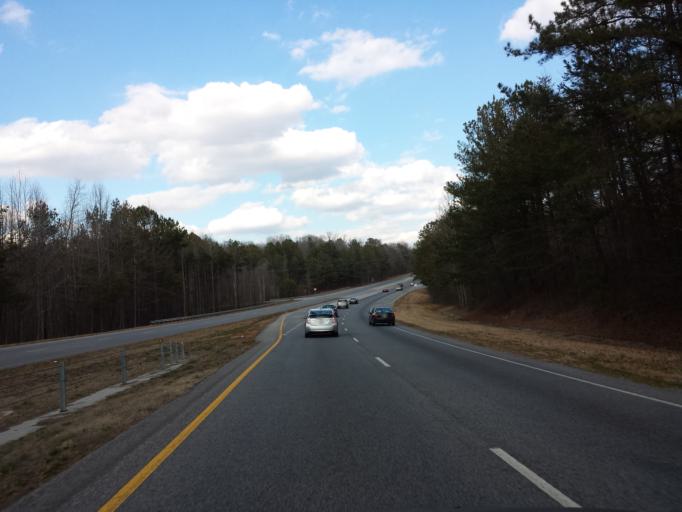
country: US
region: Georgia
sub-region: Dawson County
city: Dawsonville
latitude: 34.3943
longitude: -84.0177
